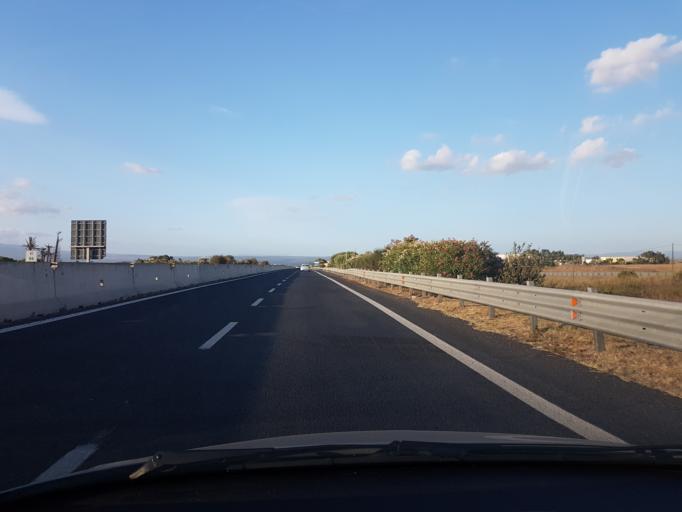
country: IT
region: Sardinia
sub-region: Provincia di Oristano
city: Siamaggiore
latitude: 39.9655
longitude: 8.6212
